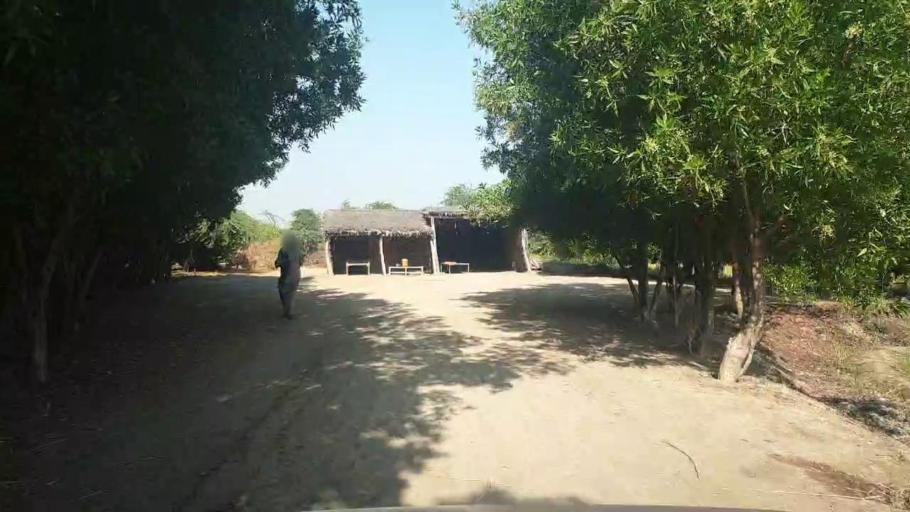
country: PK
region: Sindh
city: Tando Bago
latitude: 24.7419
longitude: 68.8855
